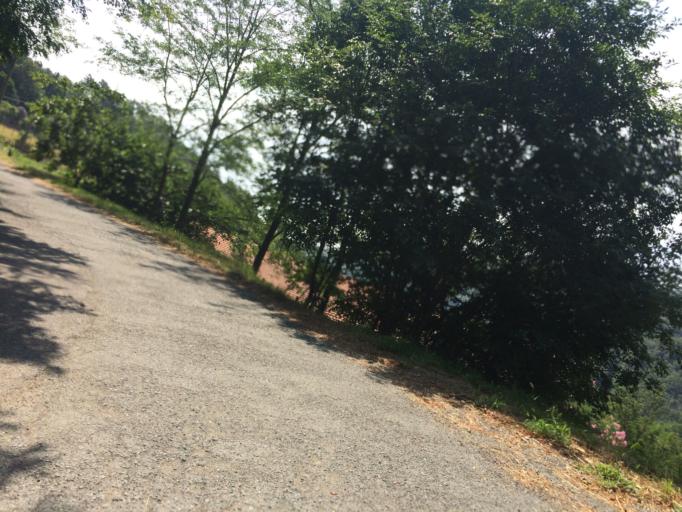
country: IT
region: Liguria
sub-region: Provincia di Genova
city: Sciarborasca
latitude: 44.4037
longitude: 8.5776
